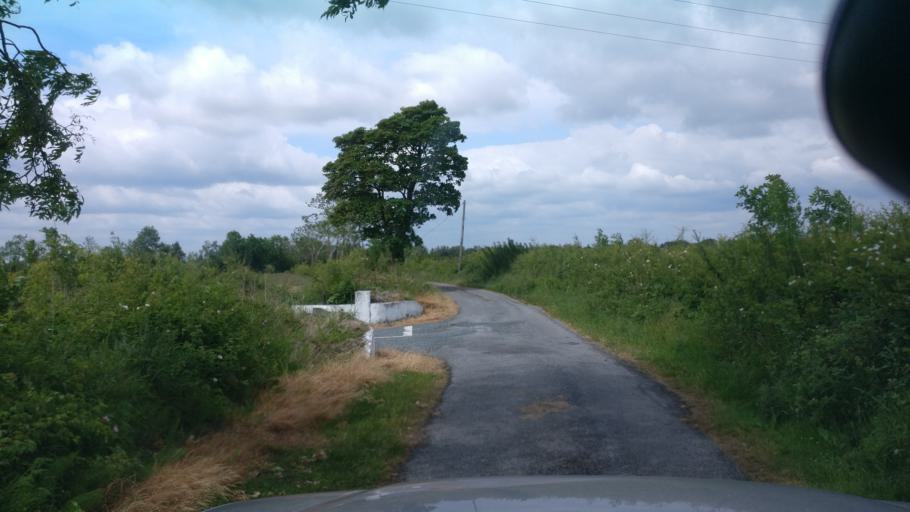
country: IE
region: Connaught
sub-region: County Galway
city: Ballinasloe
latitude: 53.2733
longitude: -8.3346
